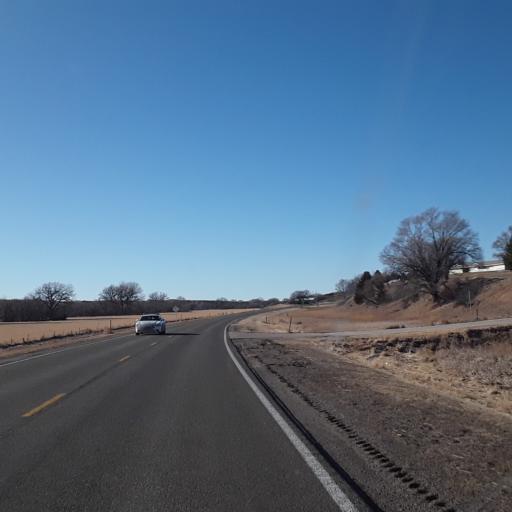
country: US
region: Nebraska
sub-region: Frontier County
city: Stockville
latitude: 40.6282
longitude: -100.5300
